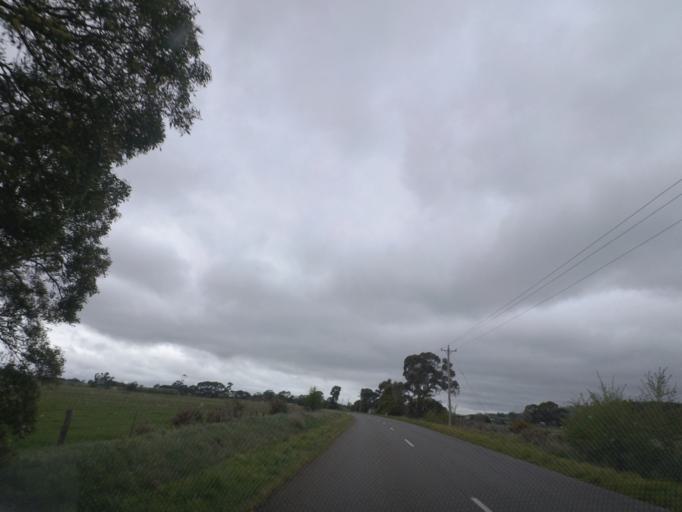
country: AU
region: Victoria
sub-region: Hume
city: Sunbury
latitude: -37.3249
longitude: 144.5561
